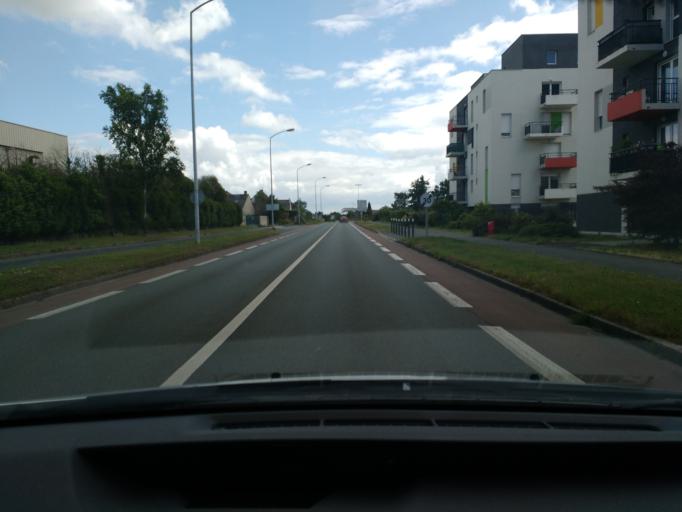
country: FR
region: Pays de la Loire
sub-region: Departement de Maine-et-Loire
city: Angers
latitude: 47.4684
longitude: -0.5060
